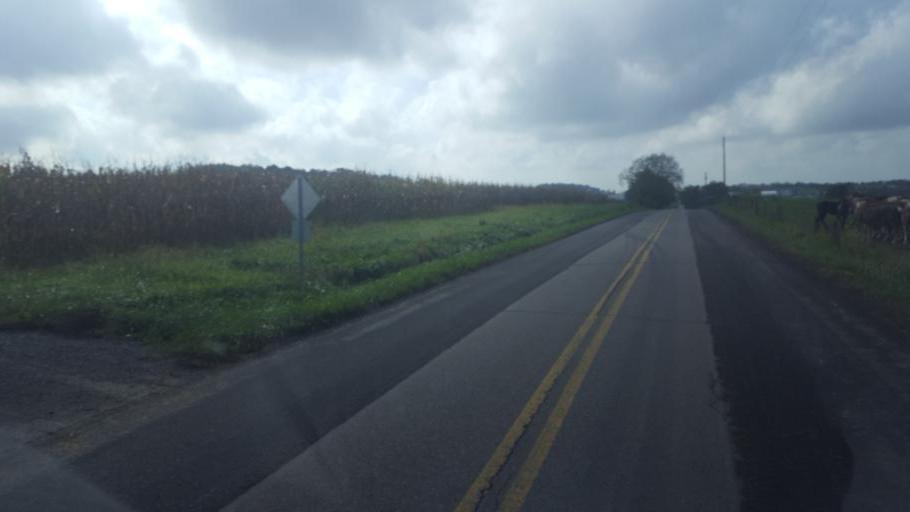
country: US
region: Ohio
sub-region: Wayne County
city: Apple Creek
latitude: 40.6456
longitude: -81.8474
